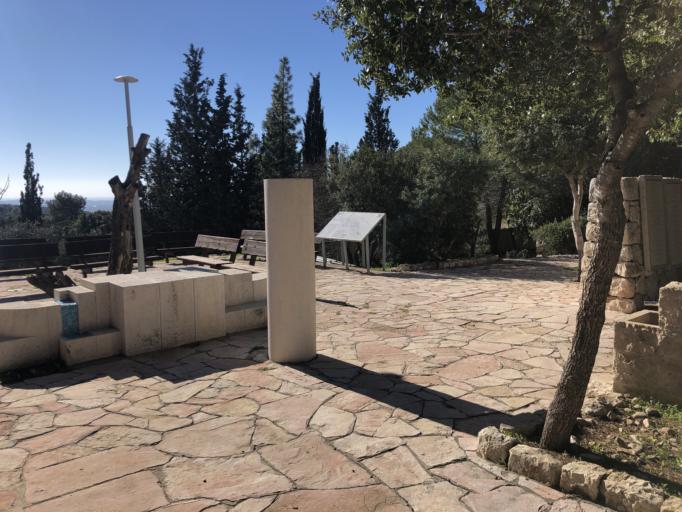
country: IL
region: Jerusalem
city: Zur Hadassa
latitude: 31.7471
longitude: 35.0479
